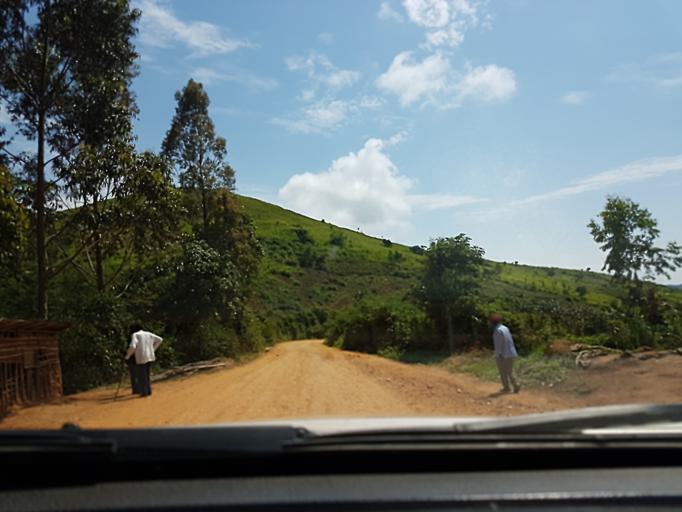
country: RW
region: Western Province
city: Cyangugu
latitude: -2.7011
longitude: 28.9185
